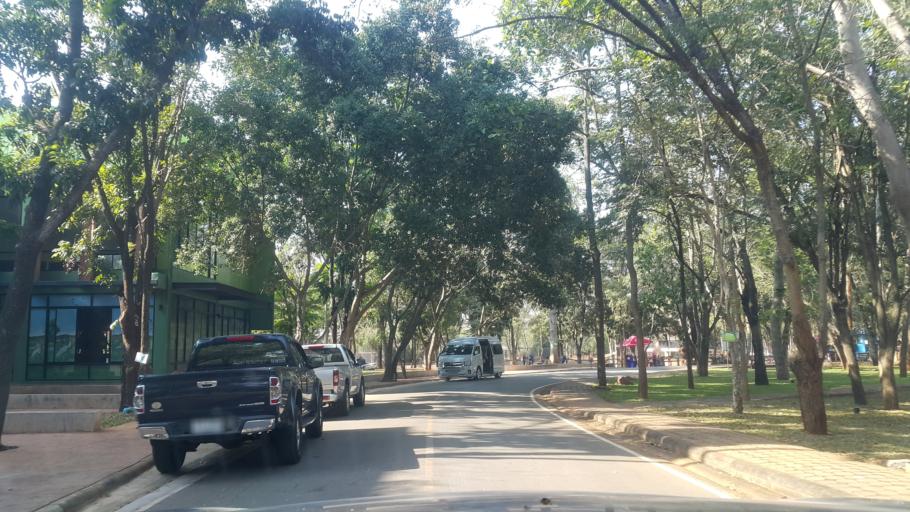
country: TH
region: Nakhon Ratchasima
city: Nakhon Ratchasima
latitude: 14.8529
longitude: 102.0864
